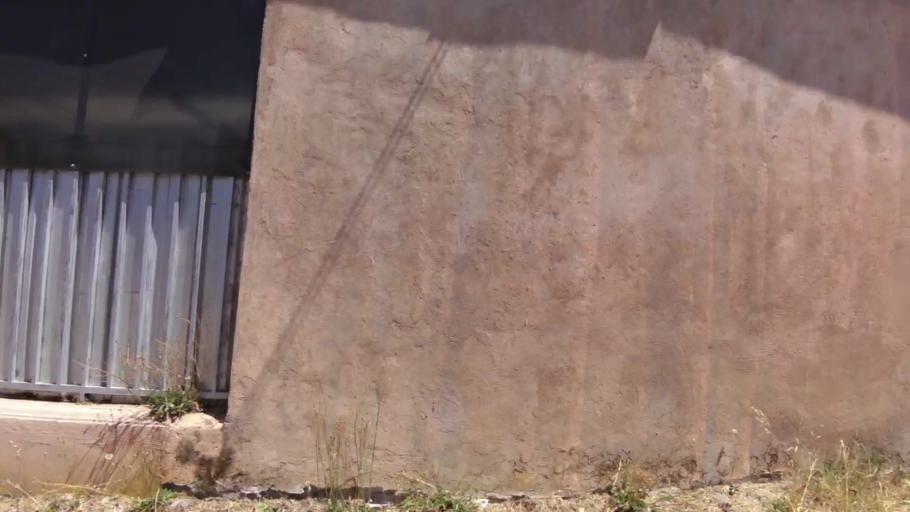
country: CL
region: Maule
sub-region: Provincia de Curico
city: Curico
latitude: -34.9824
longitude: -71.2274
